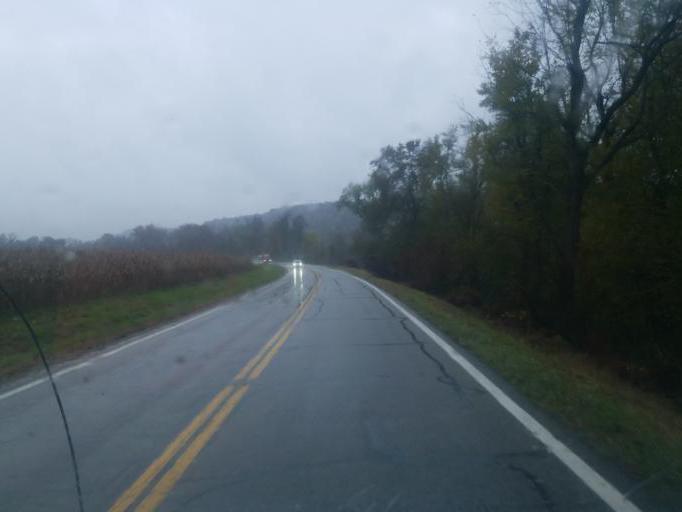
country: US
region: Ohio
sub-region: Morgan County
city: McConnelsville
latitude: 39.7846
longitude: -81.9064
